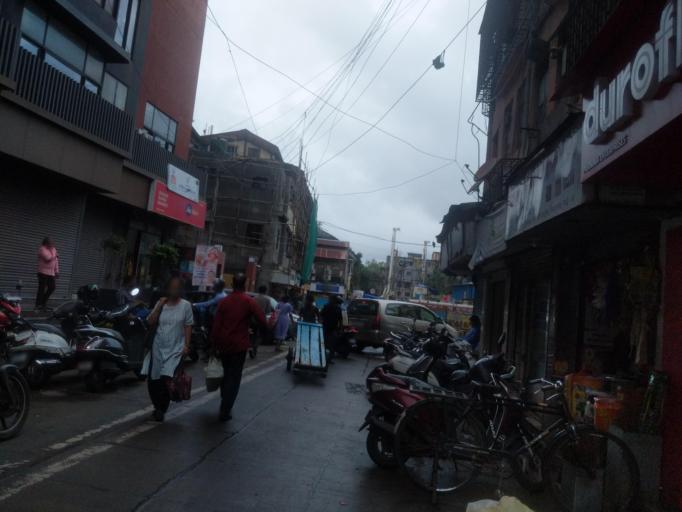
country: IN
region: Maharashtra
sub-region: Raigarh
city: Uran
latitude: 18.9474
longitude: 72.8273
